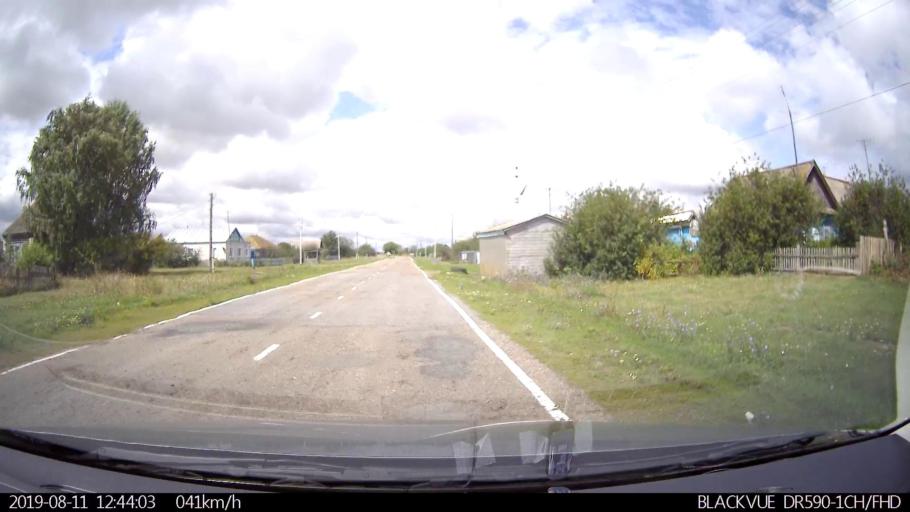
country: RU
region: Ulyanovsk
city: Ignatovka
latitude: 53.8531
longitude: 47.7390
